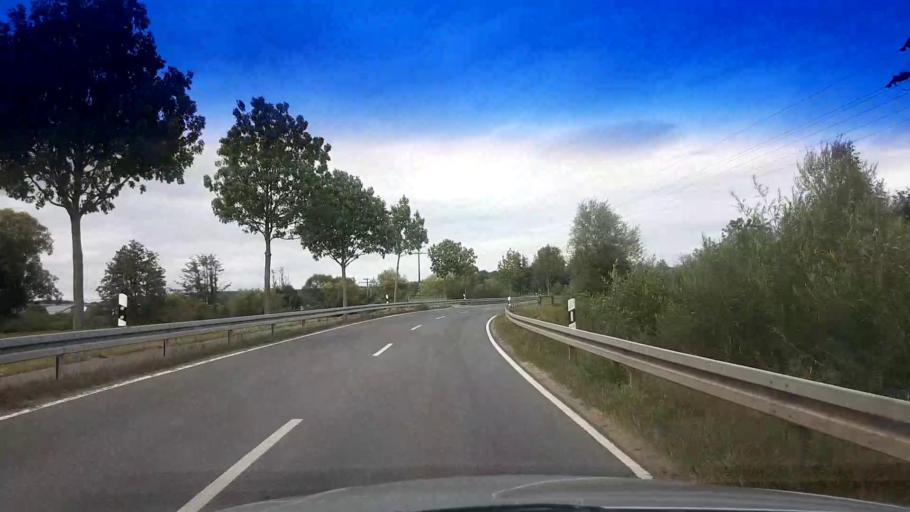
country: DE
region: Bavaria
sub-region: Upper Franconia
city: Frensdorf
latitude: 49.8188
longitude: 10.8636
